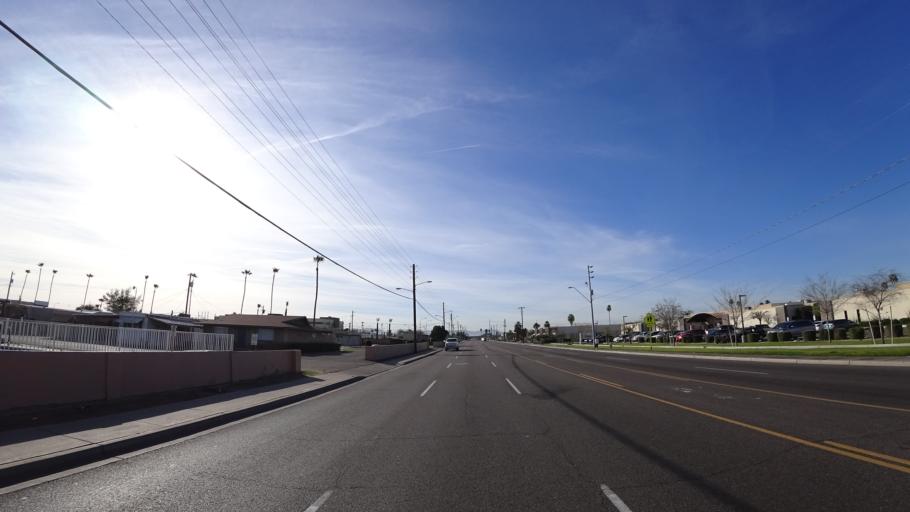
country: US
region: Arizona
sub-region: Maricopa County
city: Phoenix
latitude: 33.4935
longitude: -112.1169
